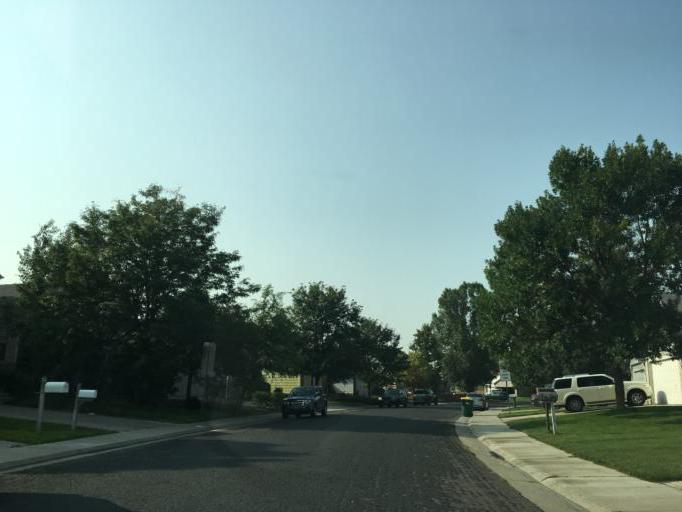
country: US
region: Colorado
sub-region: Adams County
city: Todd Creek
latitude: 39.9058
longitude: -104.8535
